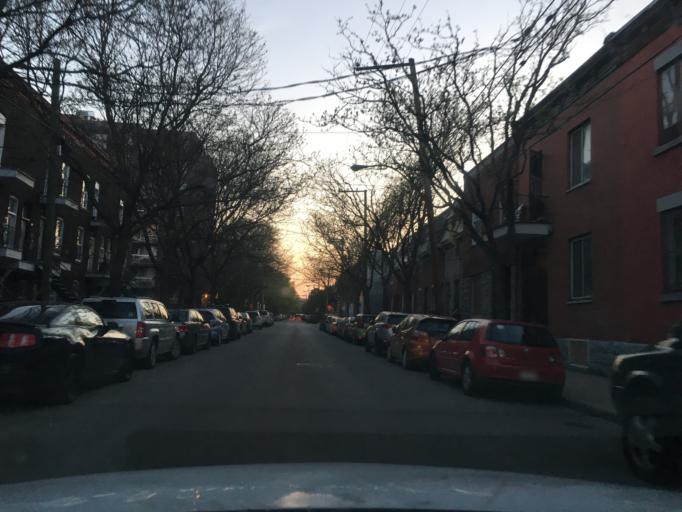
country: CA
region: Quebec
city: Westmount
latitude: 45.4786
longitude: -73.5546
